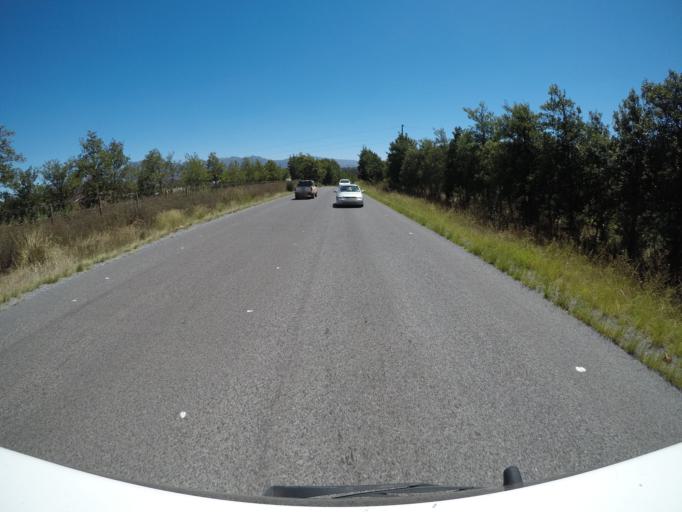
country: ZA
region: Western Cape
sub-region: Overberg District Municipality
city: Grabouw
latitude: -34.1733
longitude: 19.0343
